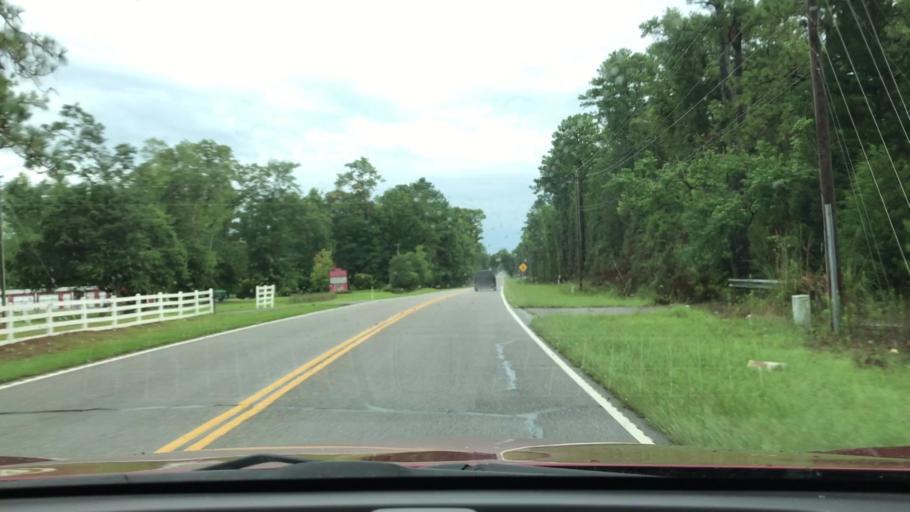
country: US
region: South Carolina
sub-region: Georgetown County
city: Georgetown
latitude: 33.4592
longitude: -79.2811
